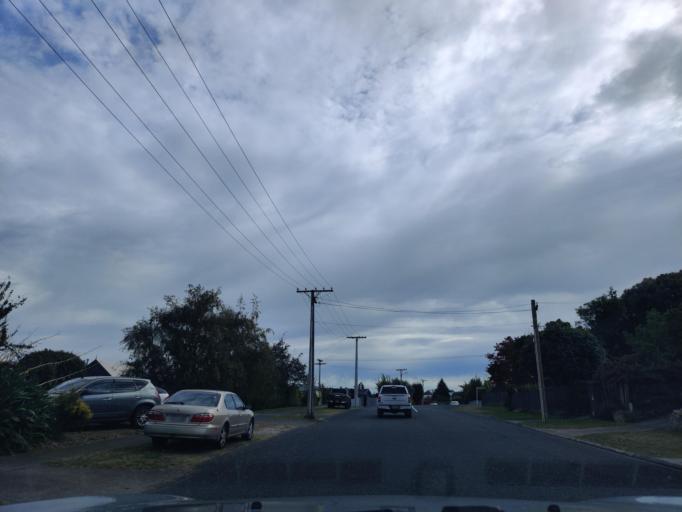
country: NZ
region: Waikato
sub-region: Taupo District
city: Taupo
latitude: -38.7091
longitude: 176.0943
